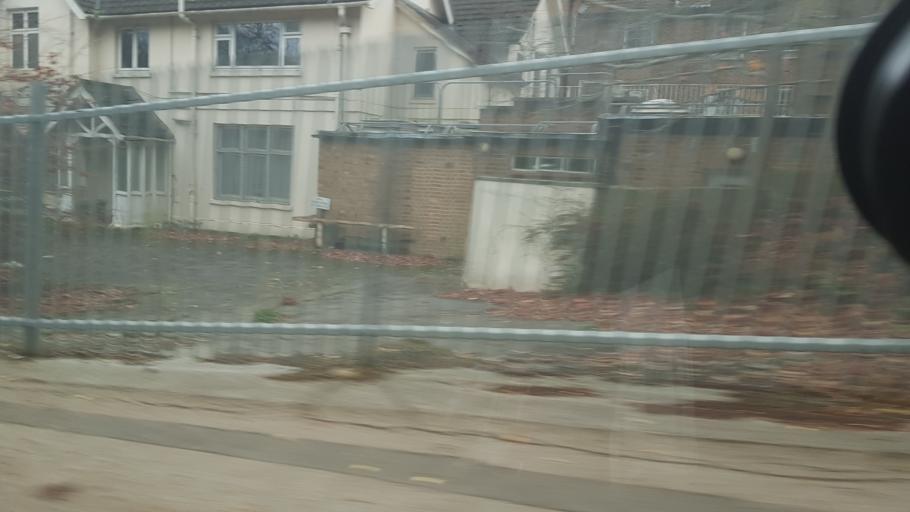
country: GB
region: England
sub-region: Bracknell Forest
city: Sandhurst
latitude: 51.3170
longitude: -0.7782
